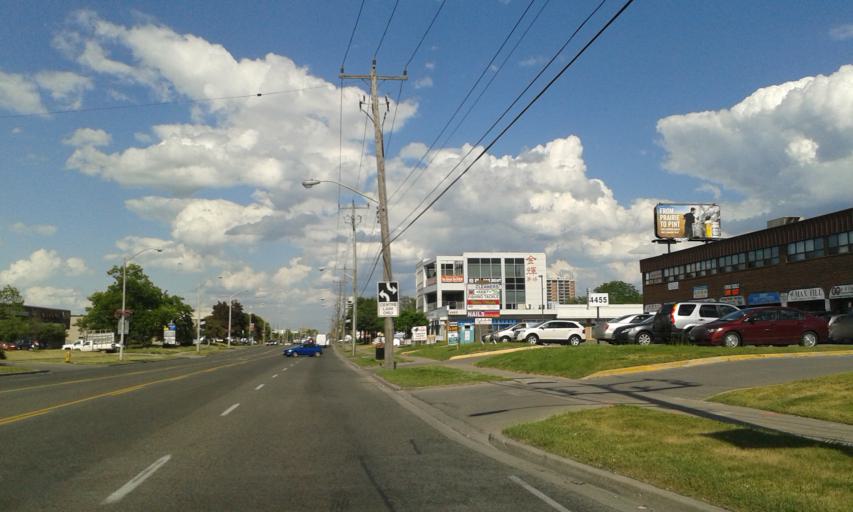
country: CA
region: Ontario
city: Scarborough
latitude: 43.7877
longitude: -79.2675
